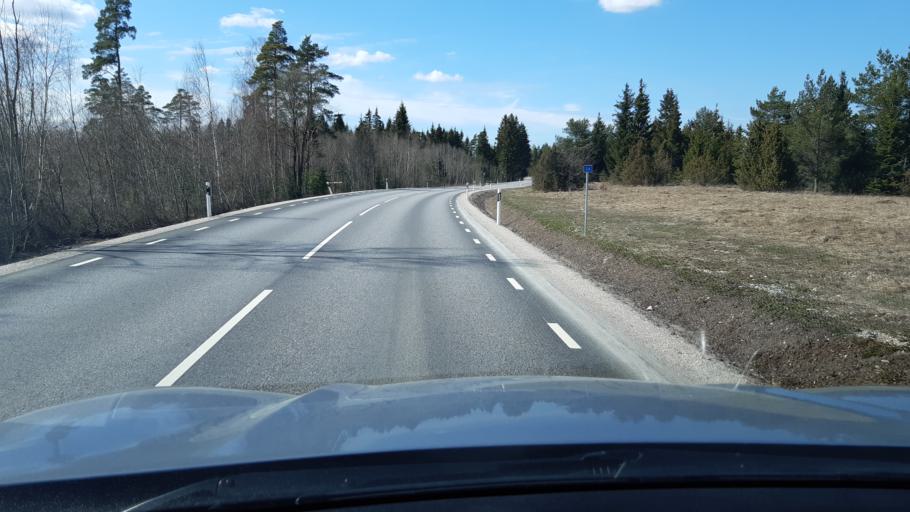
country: EE
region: Raplamaa
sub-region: Kohila vald
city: Kohila
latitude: 59.1768
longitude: 24.8295
